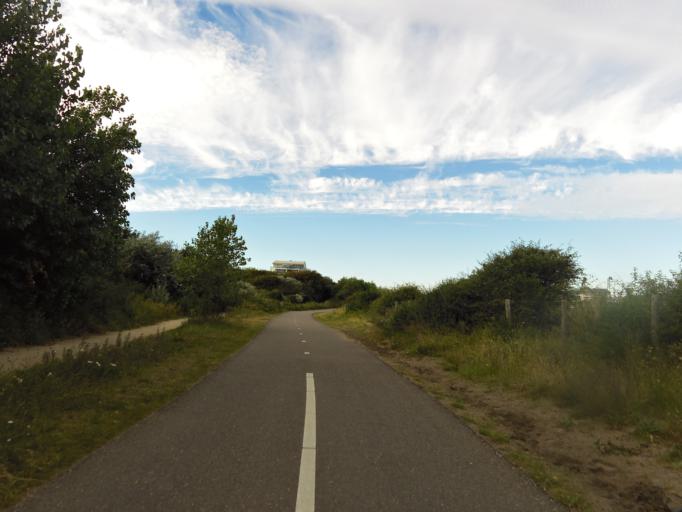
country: NL
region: South Holland
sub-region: Gemeente Katwijk
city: Katwijk aan Zee
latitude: 52.1933
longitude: 4.3862
